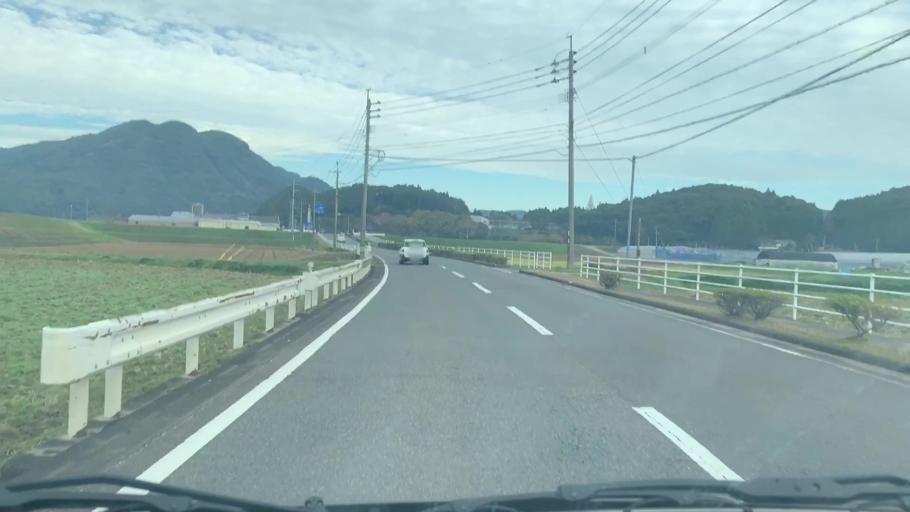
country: JP
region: Saga Prefecture
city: Imaricho-ko
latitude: 33.2973
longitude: 129.9702
